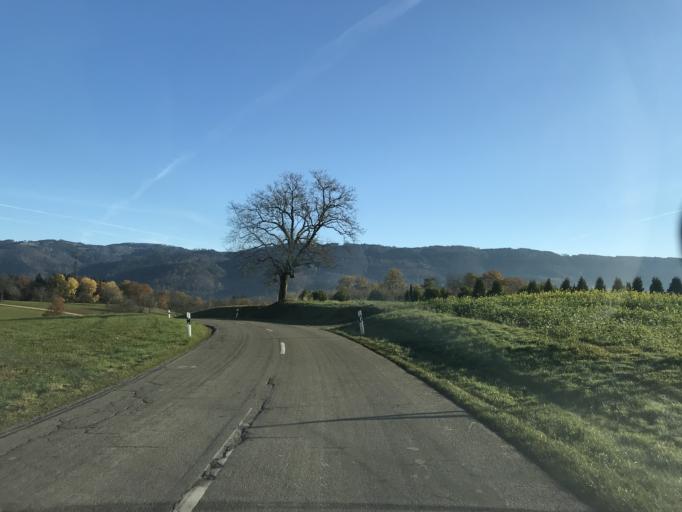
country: DE
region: Baden-Wuerttemberg
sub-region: Freiburg Region
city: Wehr
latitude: 47.6244
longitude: 7.8834
